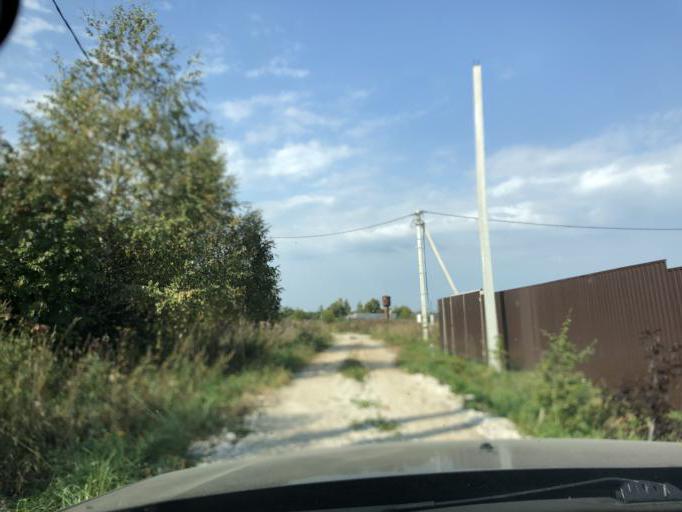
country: RU
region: Moskovskaya
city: L'vovskiy
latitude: 55.3439
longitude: 37.4521
